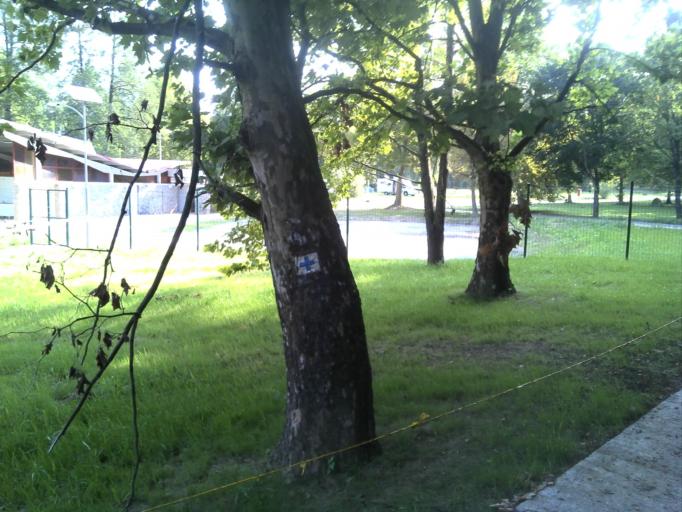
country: HU
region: Baranya
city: Pellerd
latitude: 46.1368
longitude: 18.1174
